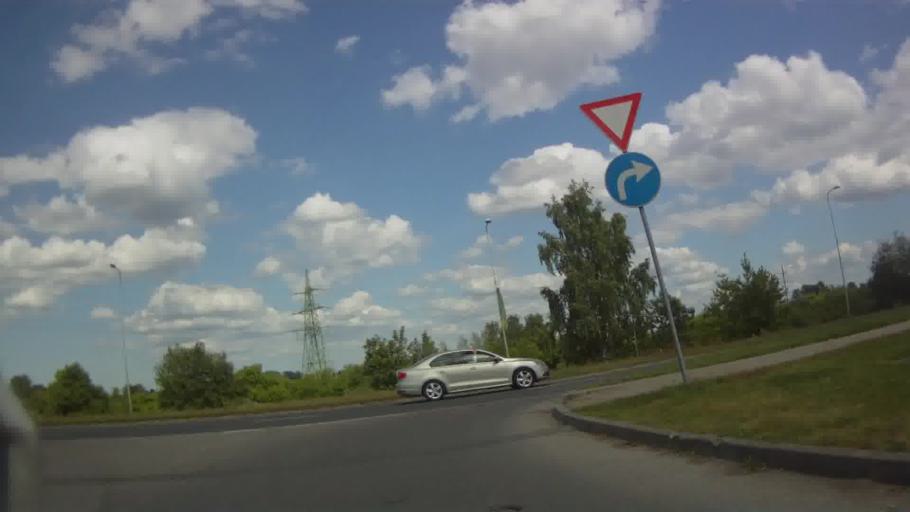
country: LV
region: Riga
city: Riga
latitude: 56.9223
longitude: 24.1083
